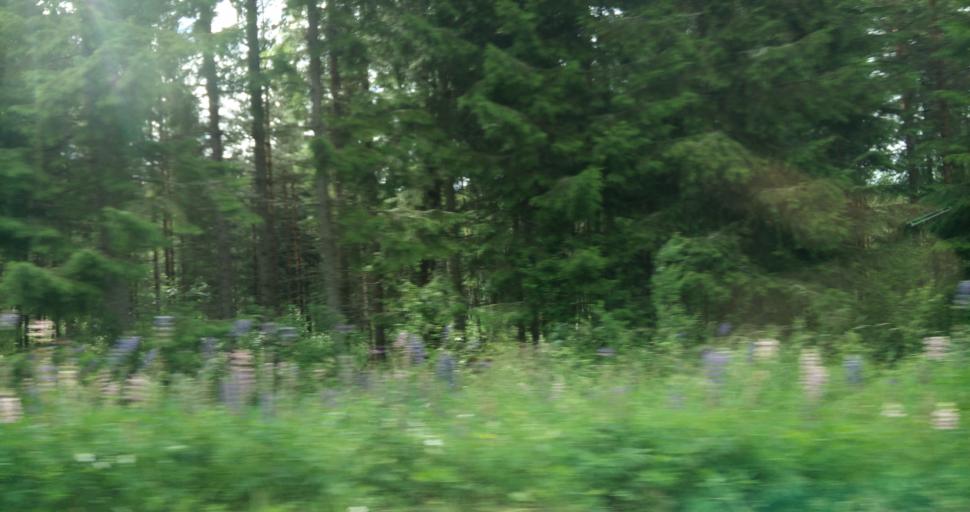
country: SE
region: Vaermland
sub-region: Hagfors Kommun
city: Ekshaerad
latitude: 60.0319
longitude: 13.4861
